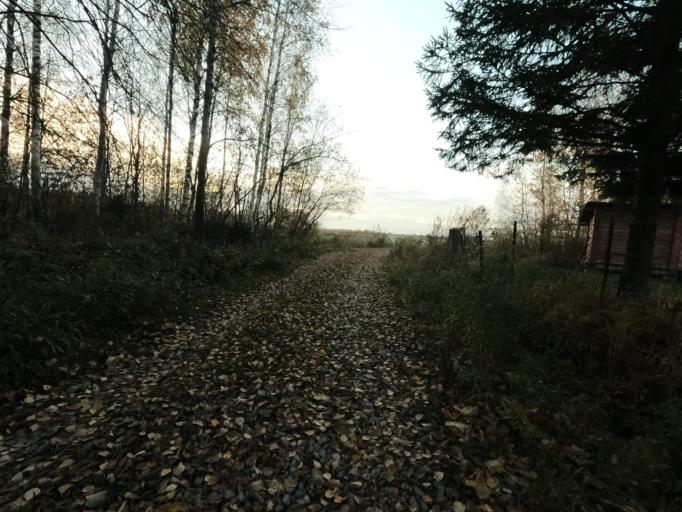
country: RU
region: Leningrad
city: Mga
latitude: 59.7828
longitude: 31.1967
